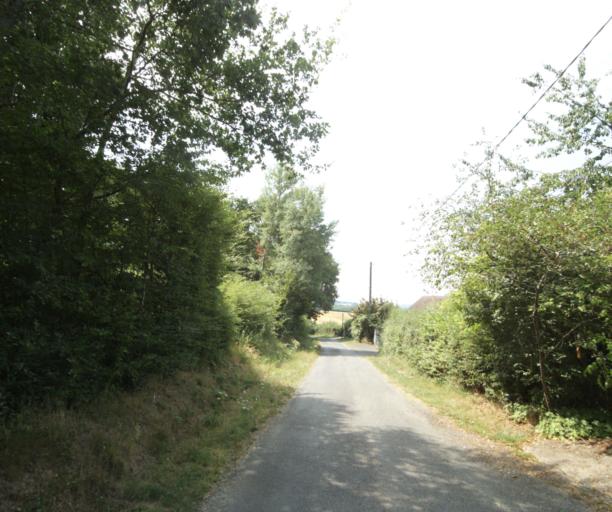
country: FR
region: Bourgogne
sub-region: Departement de Saone-et-Loire
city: Gueugnon
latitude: 46.5886
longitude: 4.0767
